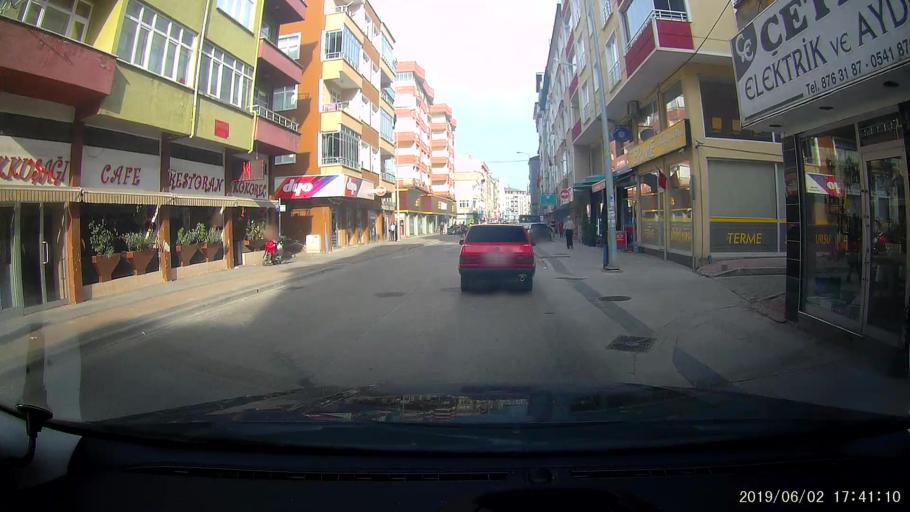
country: TR
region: Samsun
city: Terme
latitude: 41.2106
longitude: 36.9689
